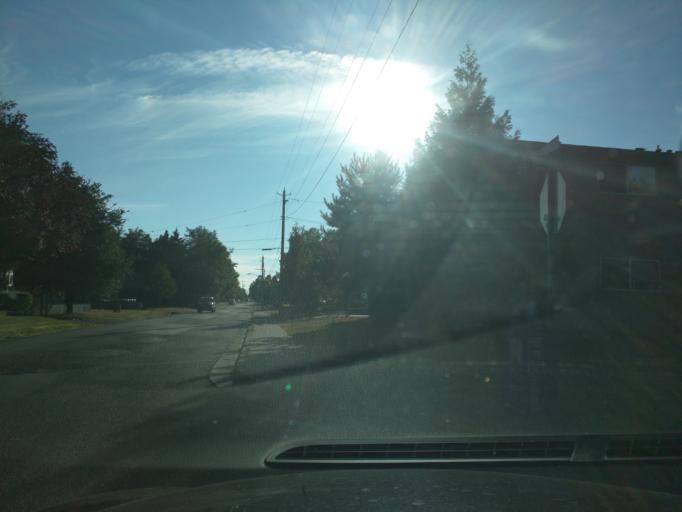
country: US
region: Washington
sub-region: Whatcom County
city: Bellingham
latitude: 48.7618
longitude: -122.4504
